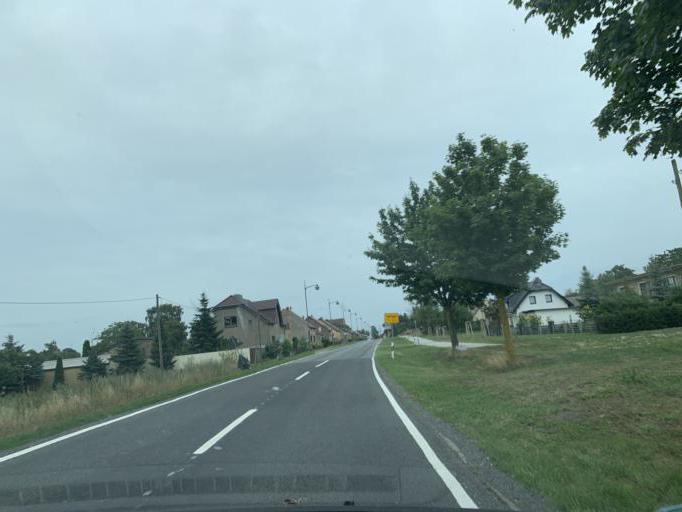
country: DE
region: Brandenburg
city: Gransee
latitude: 52.9981
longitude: 13.2440
